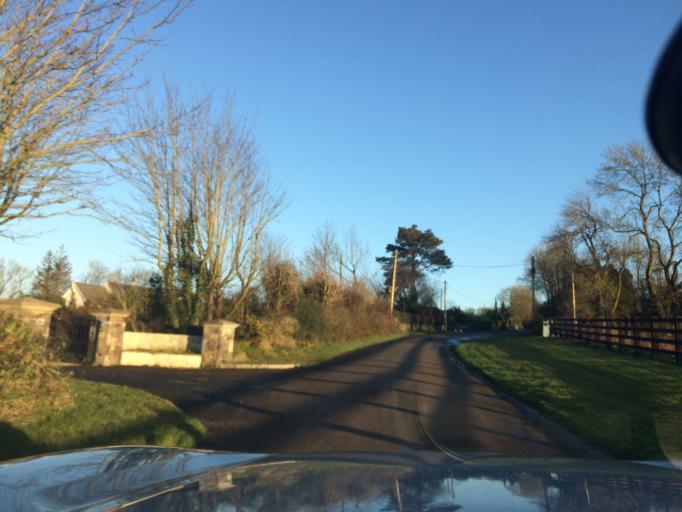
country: IE
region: Munster
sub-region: Waterford
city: Tra Mhor
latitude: 52.2323
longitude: -7.1909
